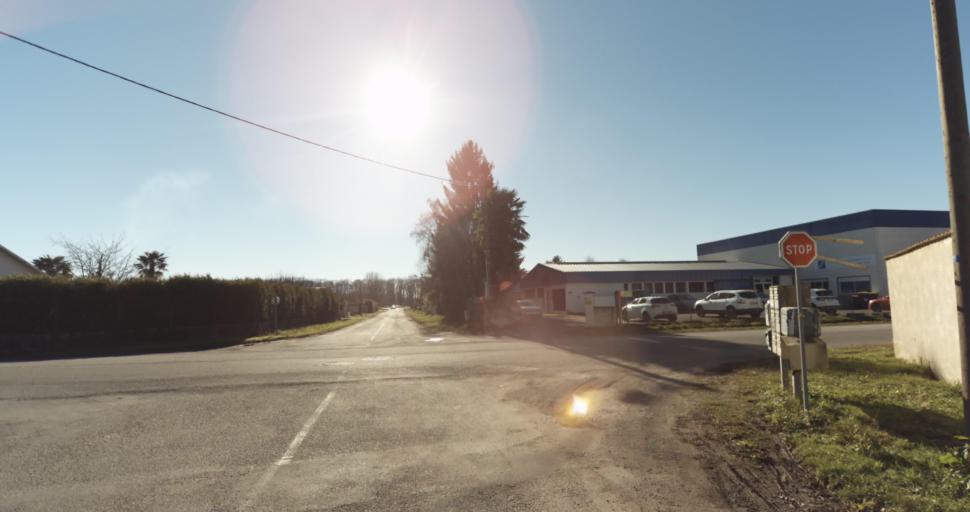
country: FR
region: Aquitaine
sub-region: Departement des Pyrenees-Atlantiques
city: Buros
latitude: 43.3277
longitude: -0.3036
